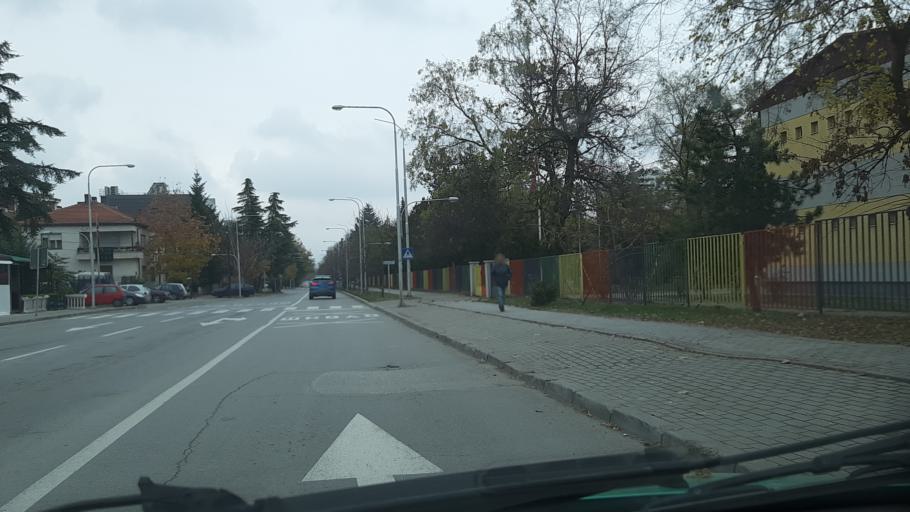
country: MK
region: Karpos
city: Skopje
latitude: 41.9893
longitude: 21.4393
